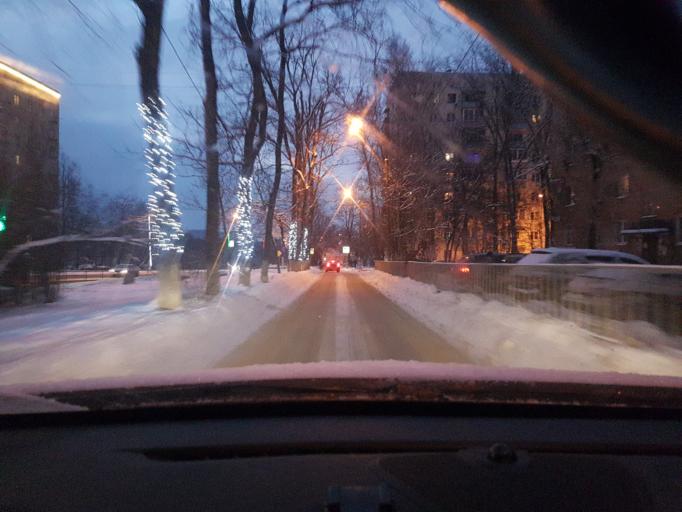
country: RU
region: Moskovskaya
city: Istra
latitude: 55.9108
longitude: 36.8725
